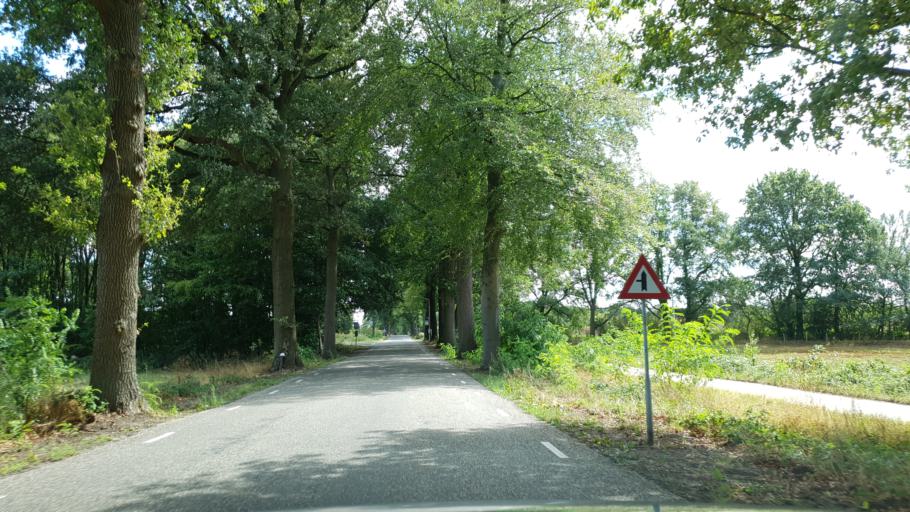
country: NL
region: Gelderland
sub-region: Gemeente Nijmegen
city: Lindenholt
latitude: 51.7896
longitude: 5.8023
